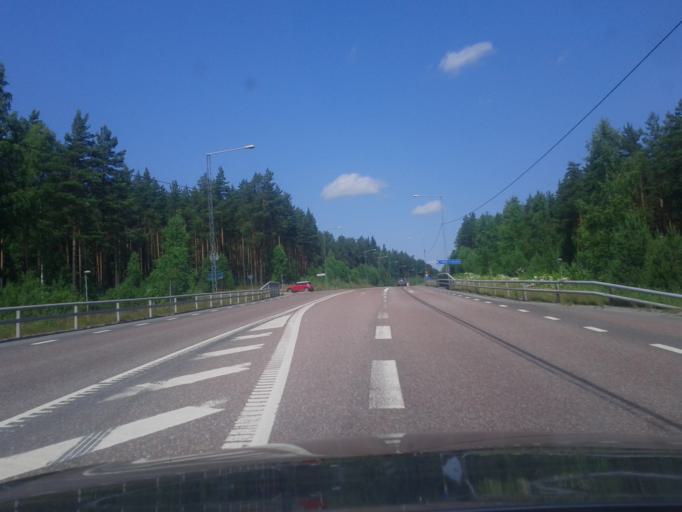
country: SE
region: Stockholm
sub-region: Vallentuna Kommun
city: Vallentuna
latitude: 59.4986
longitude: 18.1006
